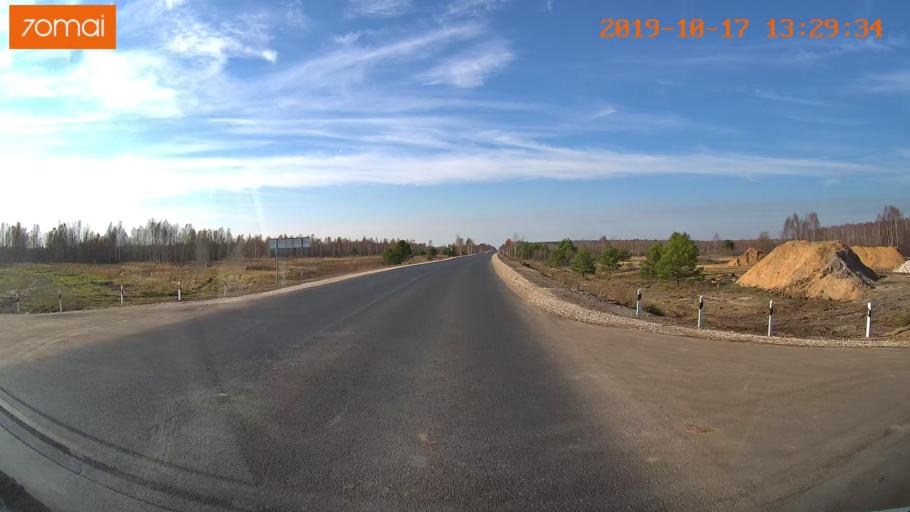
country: RU
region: Vladimir
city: Velikodvorskiy
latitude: 55.1197
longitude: 40.8377
